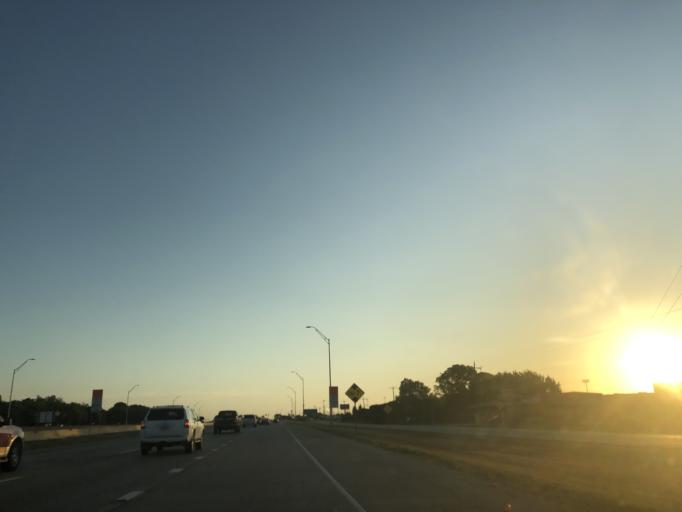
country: US
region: Texas
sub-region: Dallas County
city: Cedar Hill
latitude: 32.5809
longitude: -96.9548
